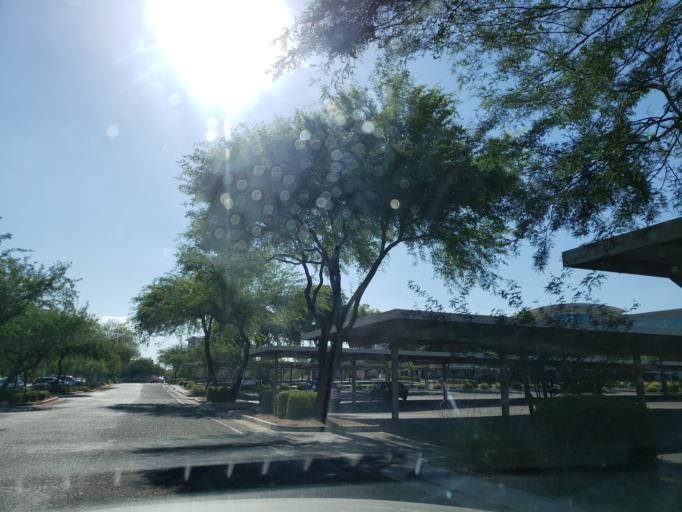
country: US
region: Arizona
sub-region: Maricopa County
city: Paradise Valley
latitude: 33.6534
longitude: -111.9320
